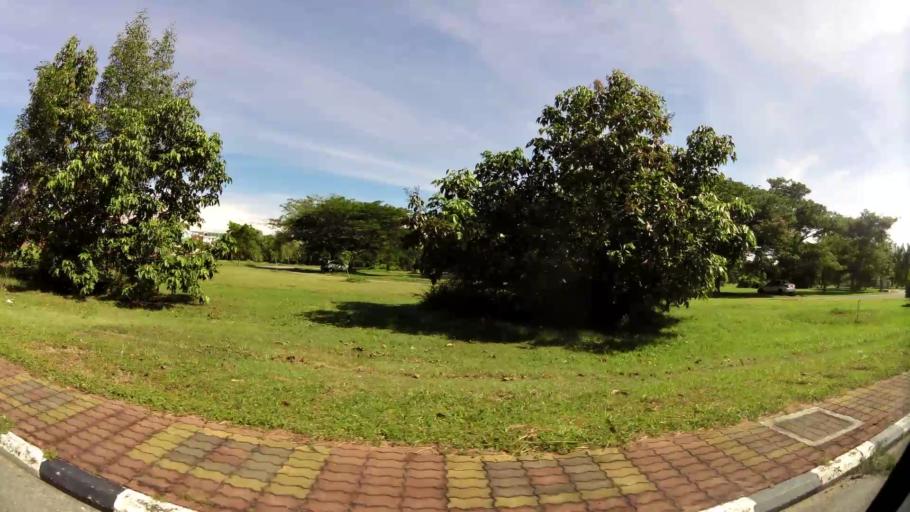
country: BN
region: Belait
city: Kuala Belait
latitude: 4.5884
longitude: 114.1995
